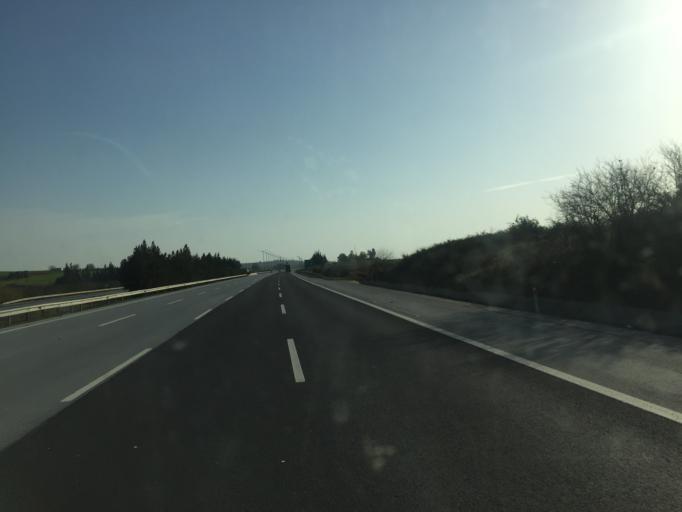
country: TR
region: Mersin
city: Yenice
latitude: 37.0230
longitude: 35.0518
